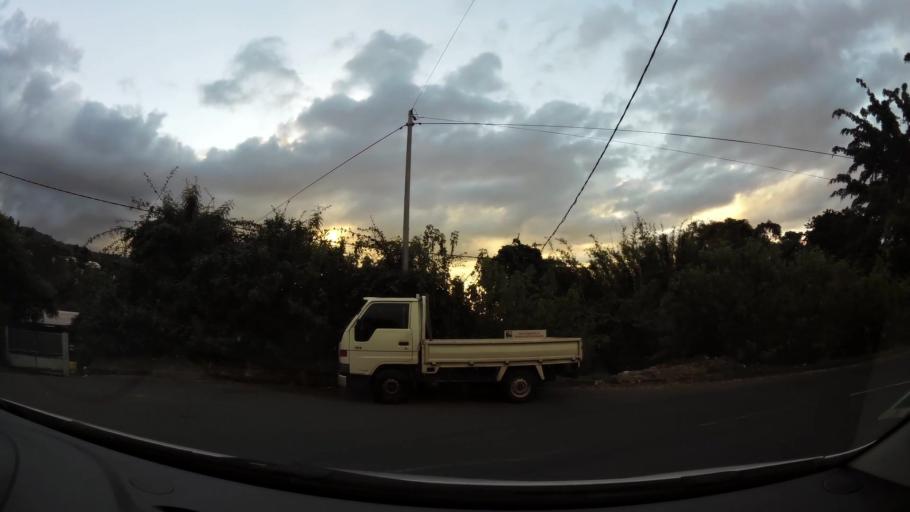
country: RE
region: Reunion
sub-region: Reunion
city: Saint-Denis
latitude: -20.9119
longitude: 55.4618
